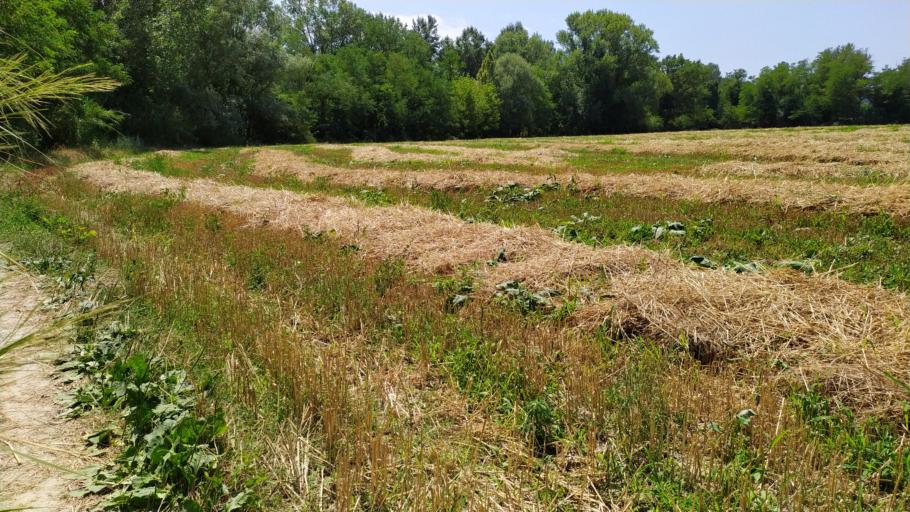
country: IT
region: Emilia-Romagna
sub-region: Forli-Cesena
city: Castrocaro Terme e Terra del Sole
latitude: 44.1900
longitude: 11.9690
